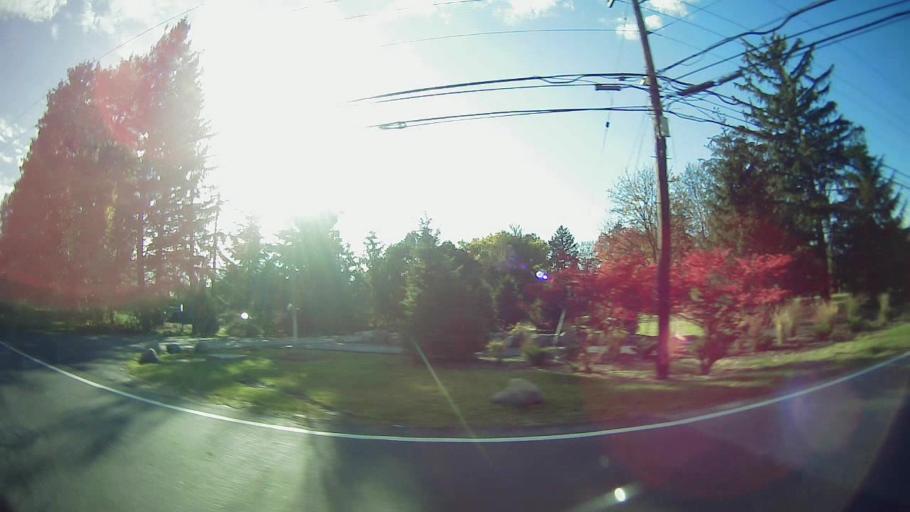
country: US
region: Michigan
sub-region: Oakland County
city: Beverly Hills
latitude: 42.5226
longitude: -83.2431
